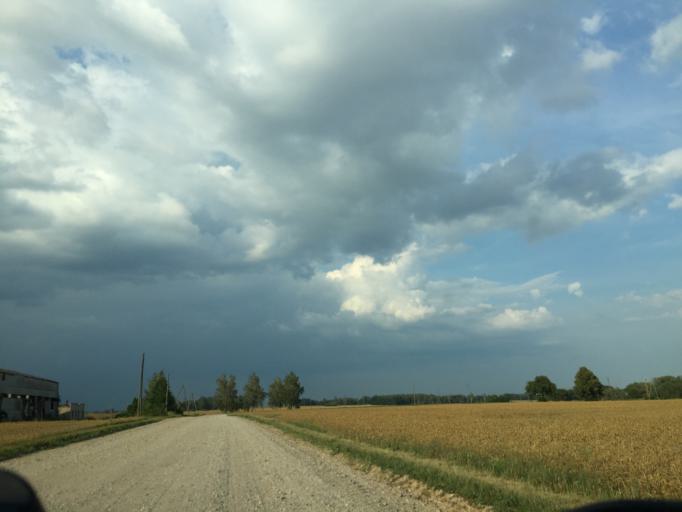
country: LV
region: Dobeles Rajons
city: Dobele
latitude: 56.5828
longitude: 23.3008
